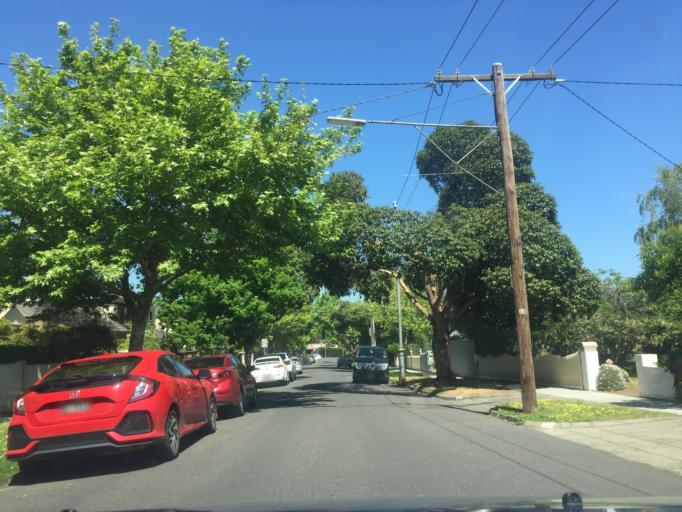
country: AU
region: Victoria
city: Balwyn
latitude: -37.8212
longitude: 145.0699
